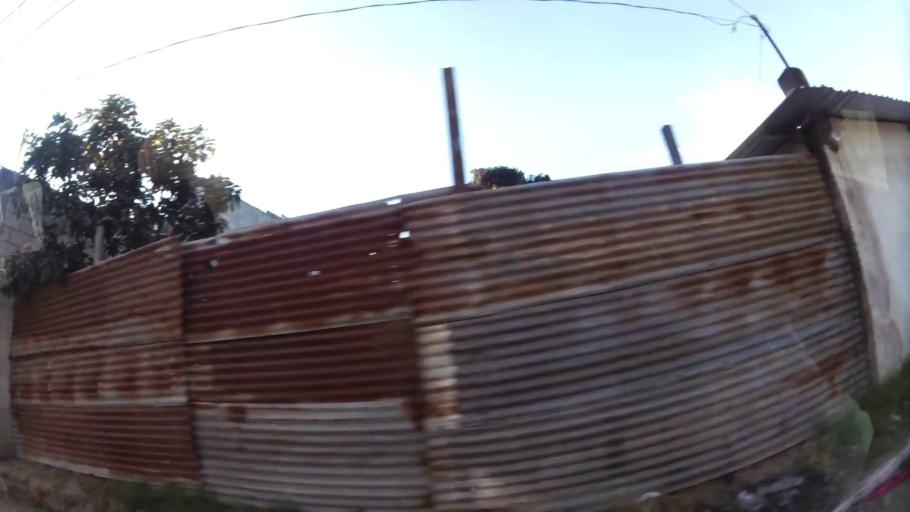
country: GT
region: Guatemala
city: Villa Nueva
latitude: 14.5167
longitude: -90.5833
